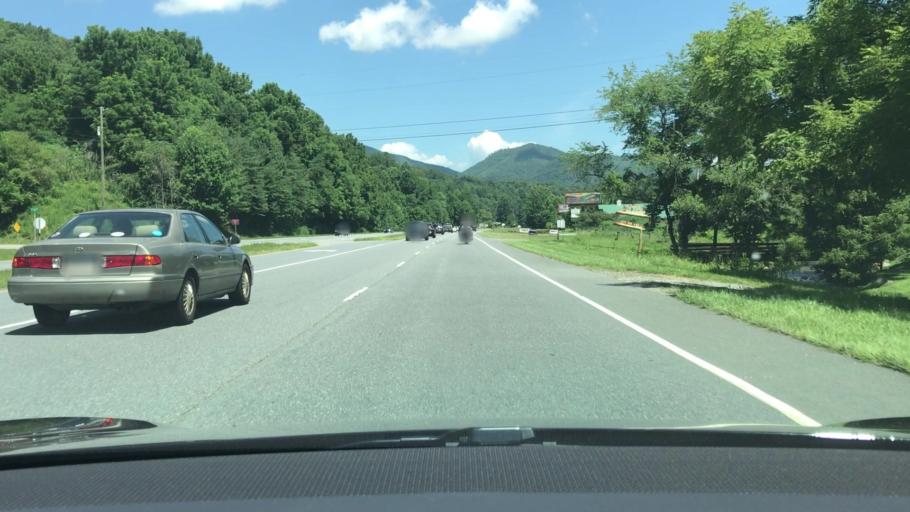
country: US
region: North Carolina
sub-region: Jackson County
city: Sylva
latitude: 35.3116
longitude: -83.2602
